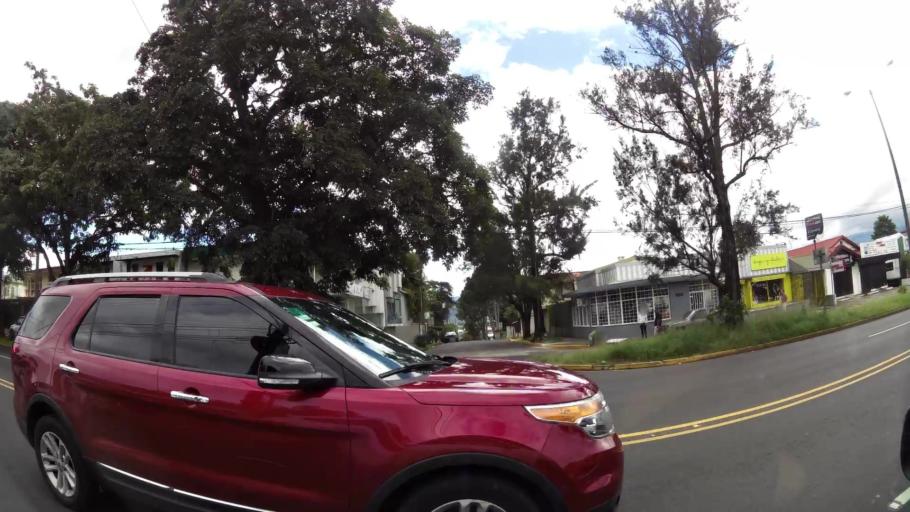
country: CR
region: San Jose
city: San Pedro
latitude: 9.9321
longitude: -84.0613
